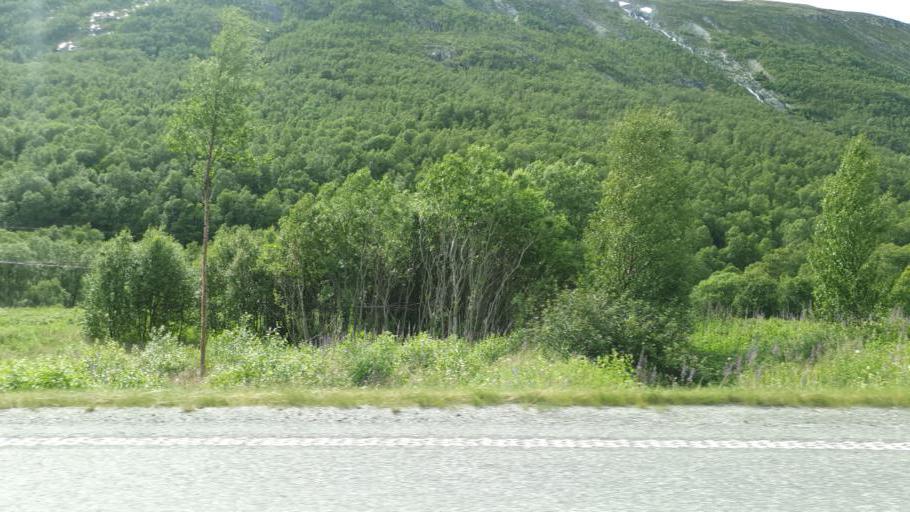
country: NO
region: Sor-Trondelag
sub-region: Oppdal
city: Oppdal
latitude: 62.4071
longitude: 9.6380
